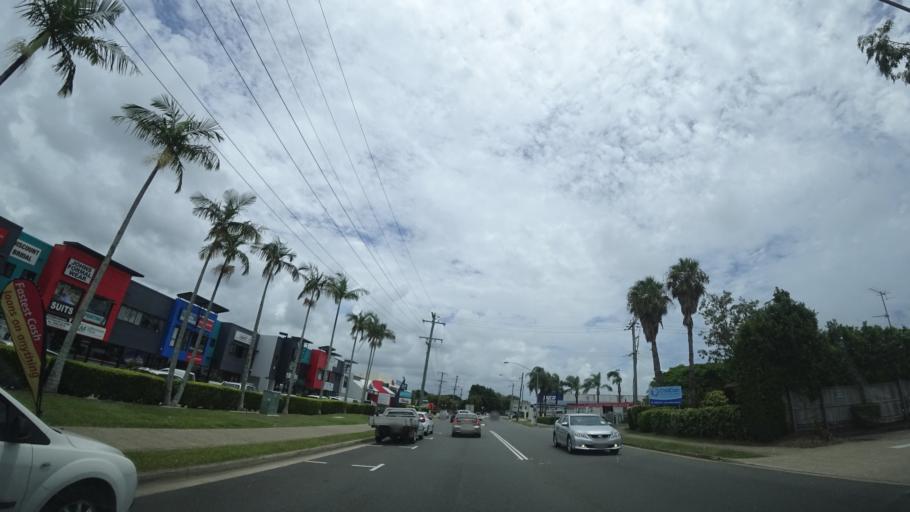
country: AU
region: Queensland
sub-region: Sunshine Coast
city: Mooloolaba
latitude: -26.6672
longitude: 153.0932
